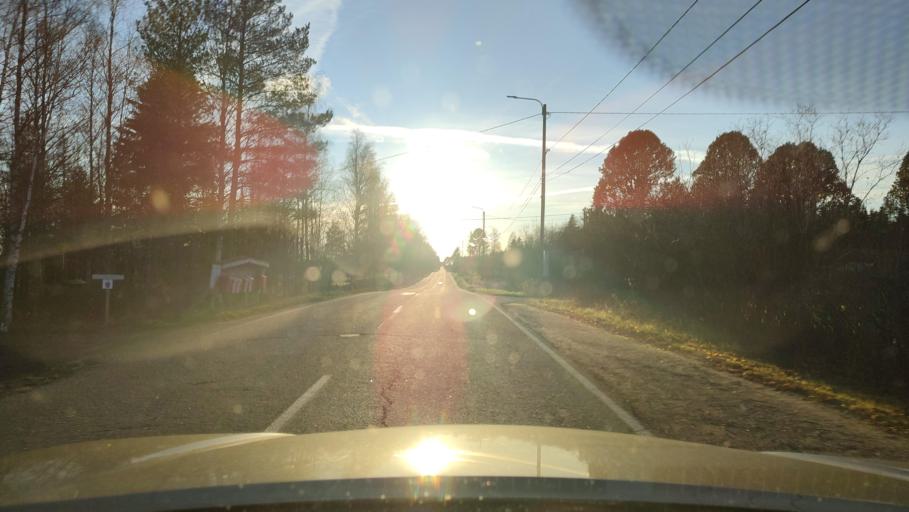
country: FI
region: Ostrobothnia
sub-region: Vaasa
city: Malax
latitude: 62.7053
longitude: 21.5968
